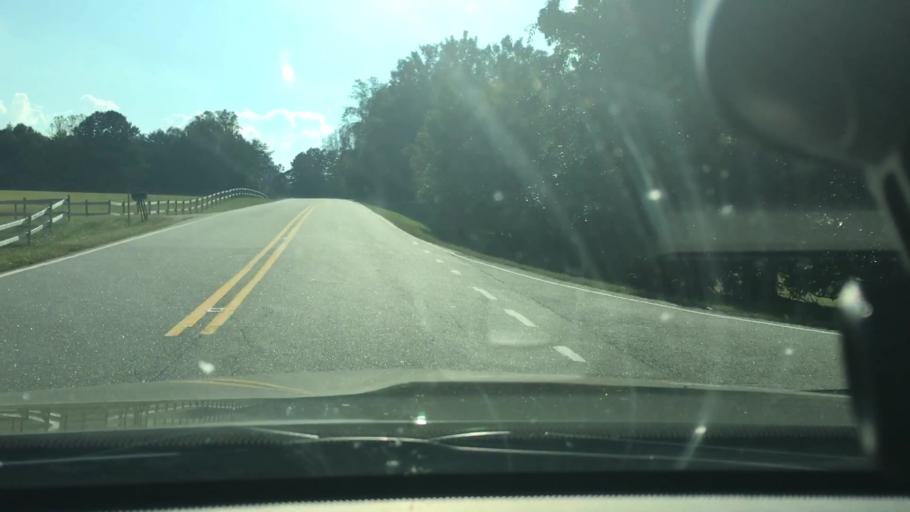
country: US
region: North Carolina
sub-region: Rutherford County
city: Rutherfordton
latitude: 35.3610
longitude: -81.9815
